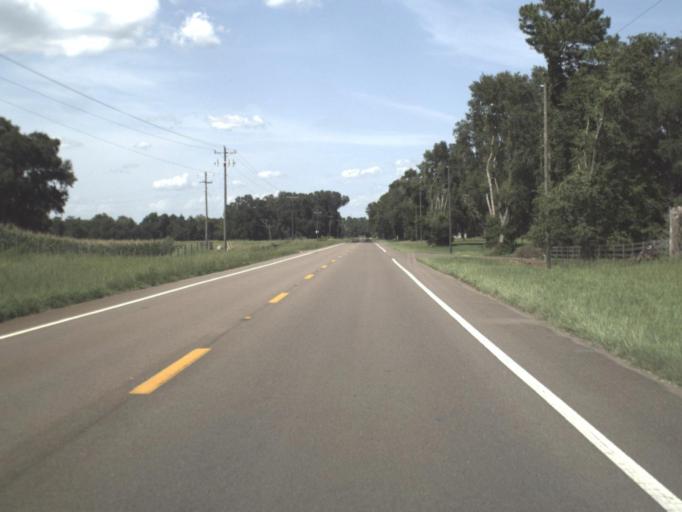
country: US
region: Florida
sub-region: Gilchrist County
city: Trenton
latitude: 29.6314
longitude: -82.8032
